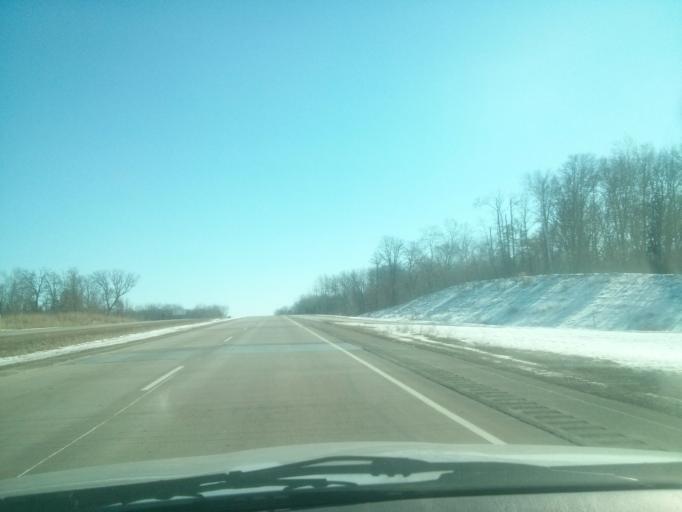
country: US
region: Wisconsin
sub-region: Saint Croix County
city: Somerset
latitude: 45.1069
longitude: -92.7212
